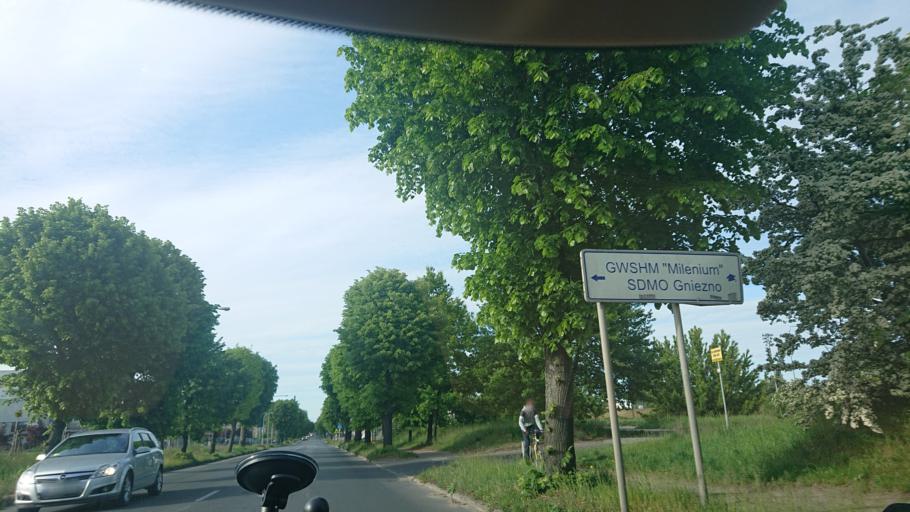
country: PL
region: Greater Poland Voivodeship
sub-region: Powiat gnieznienski
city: Gniezno
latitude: 52.5197
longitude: 17.5961
